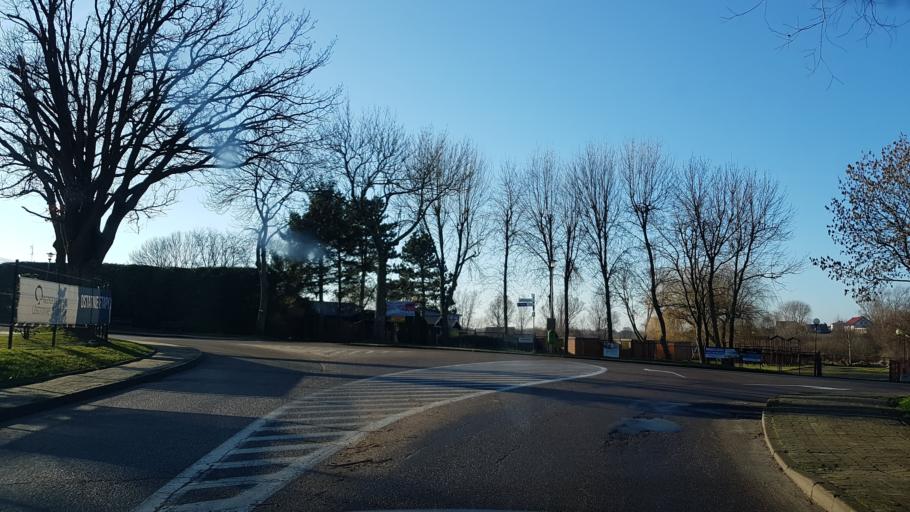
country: PL
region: West Pomeranian Voivodeship
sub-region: Powiat kolobrzeski
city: Ustronie Morskie
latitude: 54.2062
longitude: 15.7377
